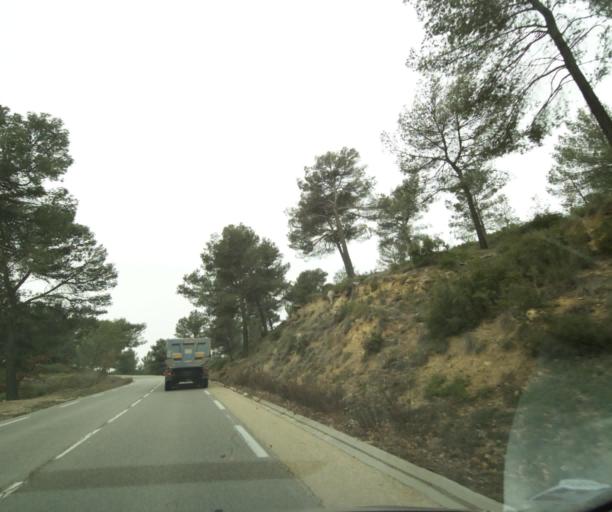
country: FR
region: Provence-Alpes-Cote d'Azur
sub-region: Departement des Bouches-du-Rhone
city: Belcodene
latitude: 43.4250
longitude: 5.6184
